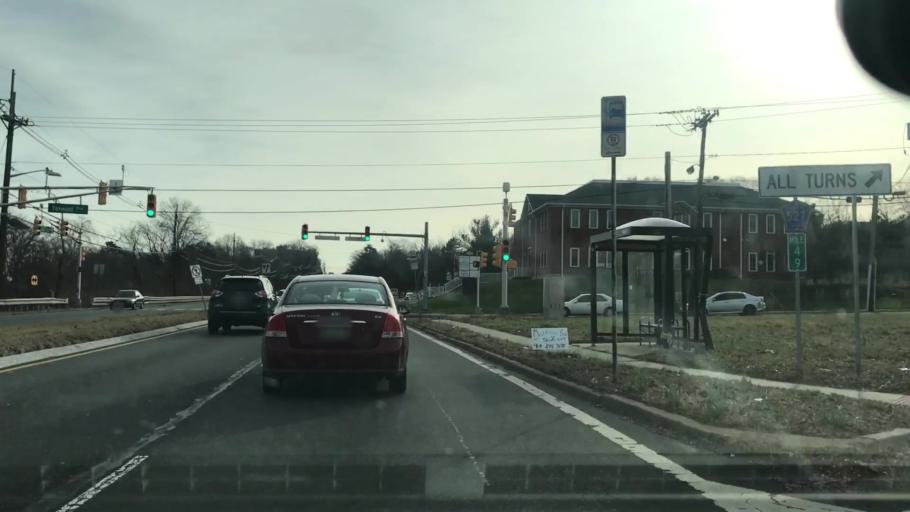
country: US
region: New Jersey
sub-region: Somerset County
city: Somerset
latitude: 40.5112
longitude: -74.4831
